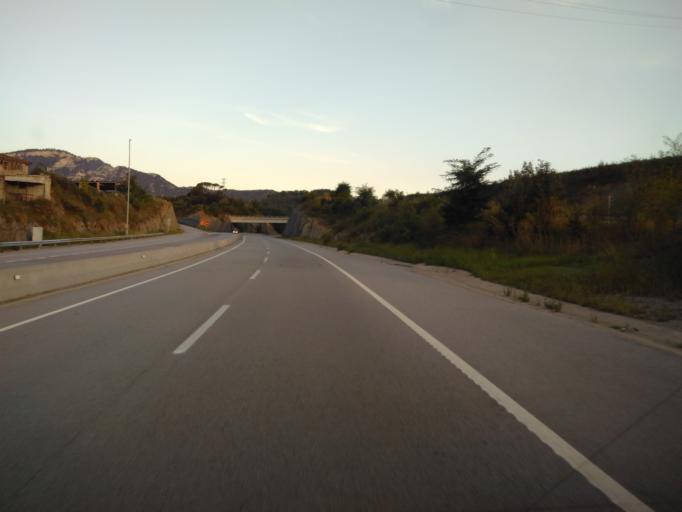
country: ES
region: Catalonia
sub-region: Provincia de Barcelona
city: Oris
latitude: 42.0780
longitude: 2.2356
